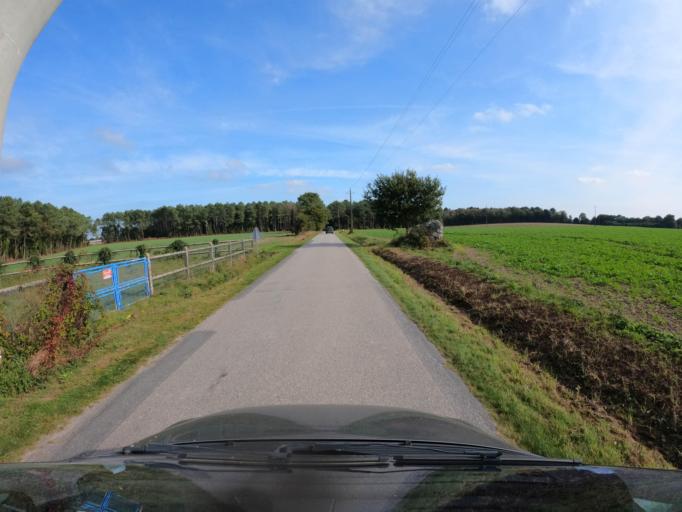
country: FR
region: Brittany
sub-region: Departement du Morbihan
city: Ploermel
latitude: 47.8804
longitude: -2.3889
